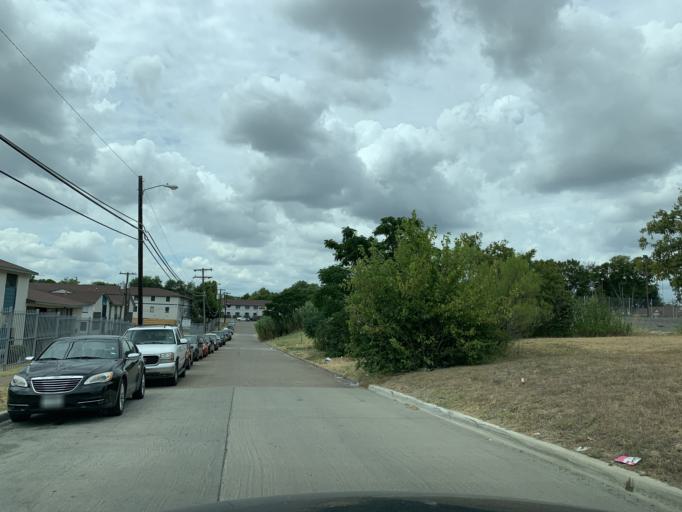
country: US
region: Texas
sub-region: Dallas County
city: Cockrell Hill
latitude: 32.7481
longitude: -96.8785
